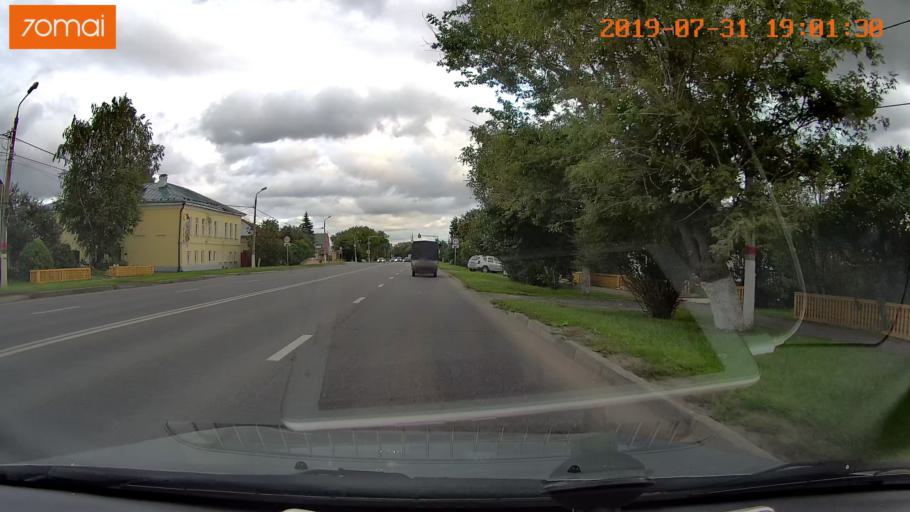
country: RU
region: Moskovskaya
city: Raduzhnyy
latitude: 55.1261
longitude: 38.7289
